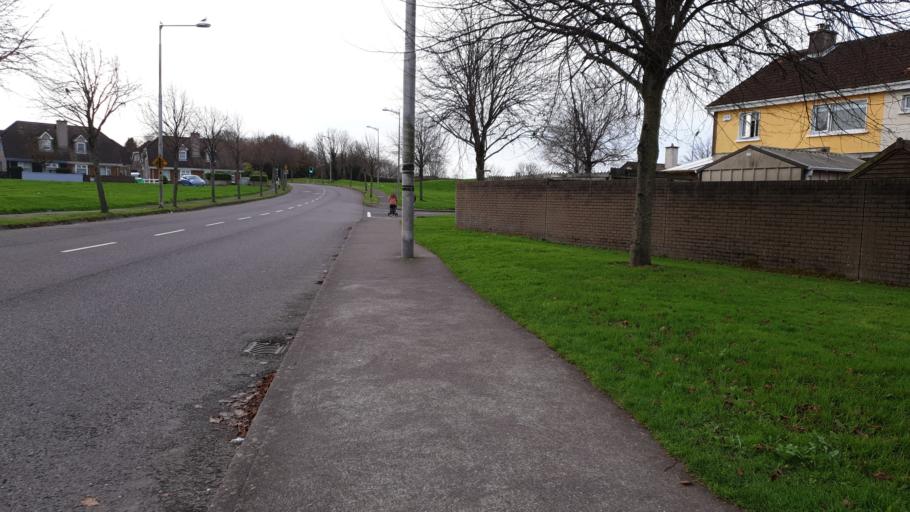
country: IE
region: Munster
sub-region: County Cork
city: Cork
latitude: 51.8933
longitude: -8.4081
